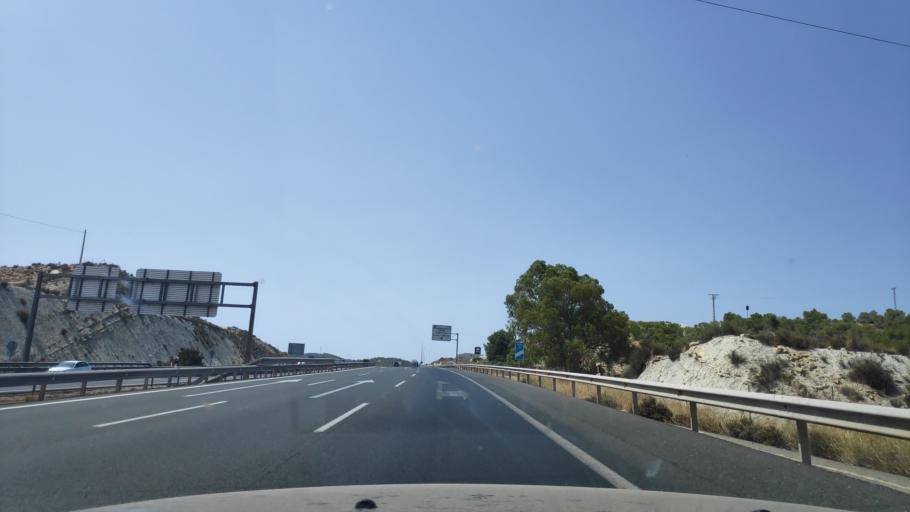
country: ES
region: Murcia
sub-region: Murcia
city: Murcia
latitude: 37.8803
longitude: -1.1319
